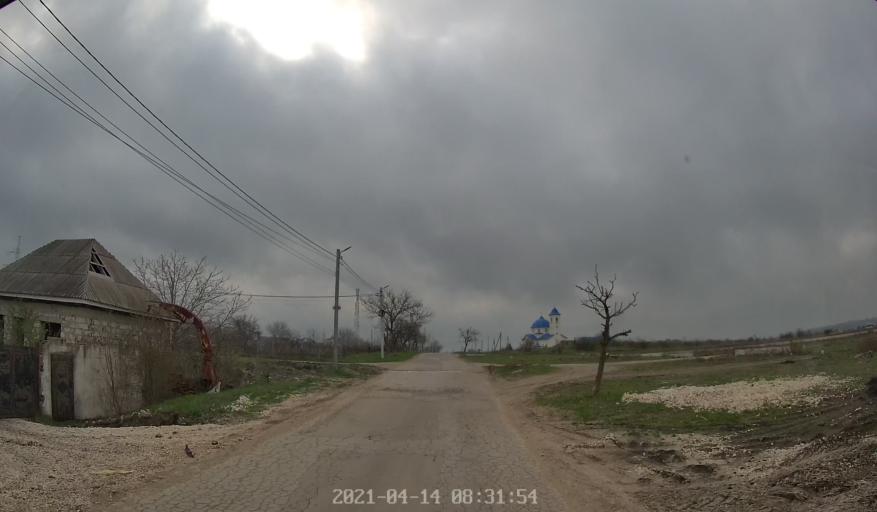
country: MD
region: Chisinau
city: Stauceni
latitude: 47.0603
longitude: 28.9373
